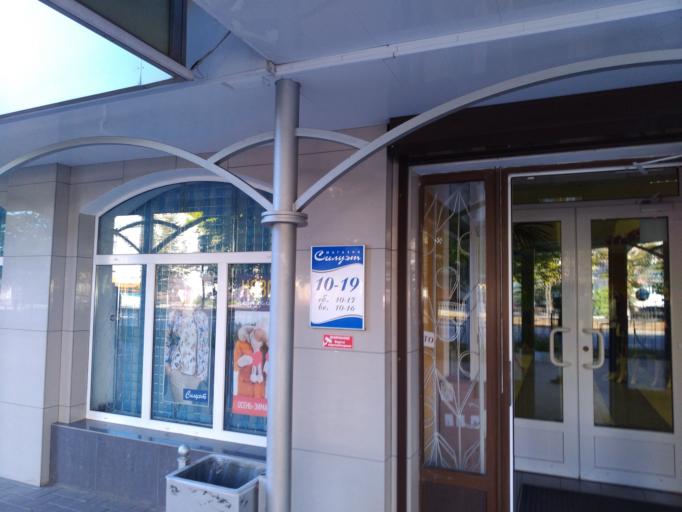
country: RU
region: Kaluga
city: Kaluga
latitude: 54.5213
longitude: 36.2688
